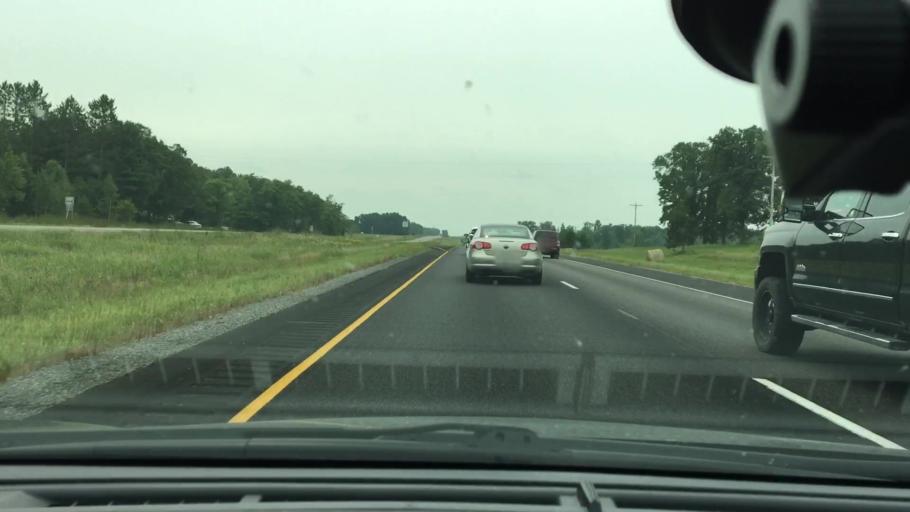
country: US
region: Minnesota
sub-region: Mille Lacs County
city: Milaca
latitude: 45.9054
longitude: -93.6634
